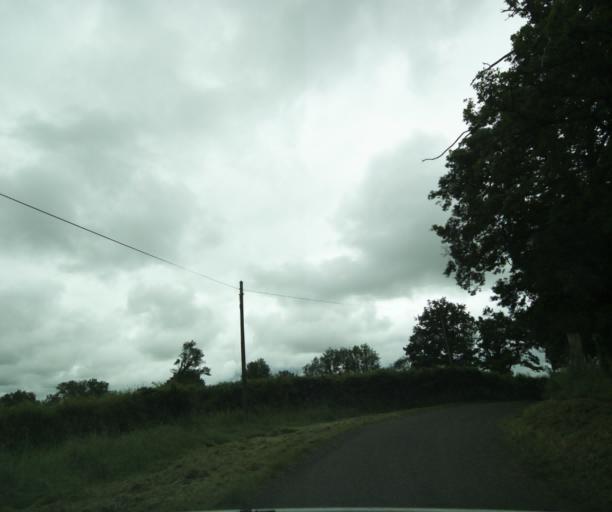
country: FR
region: Bourgogne
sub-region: Departement de Saone-et-Loire
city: Charolles
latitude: 46.4562
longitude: 4.2908
